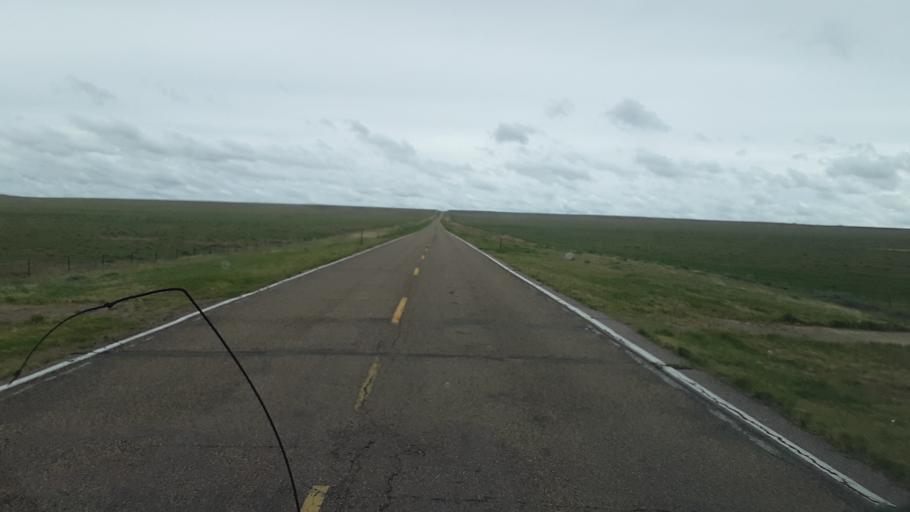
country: US
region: Colorado
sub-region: Lincoln County
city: Hugo
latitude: 38.8498
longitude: -103.3737
